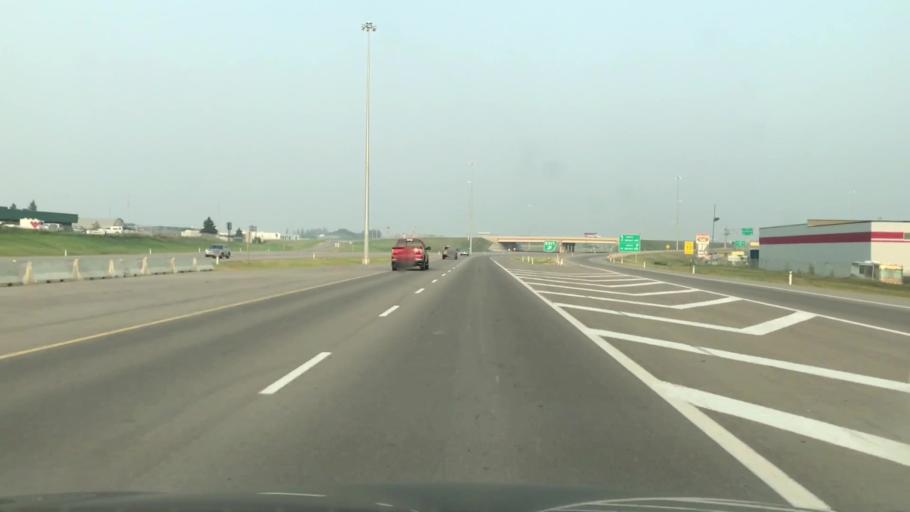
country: CA
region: Alberta
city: Sherwood Park
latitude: 53.5174
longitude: -113.3776
